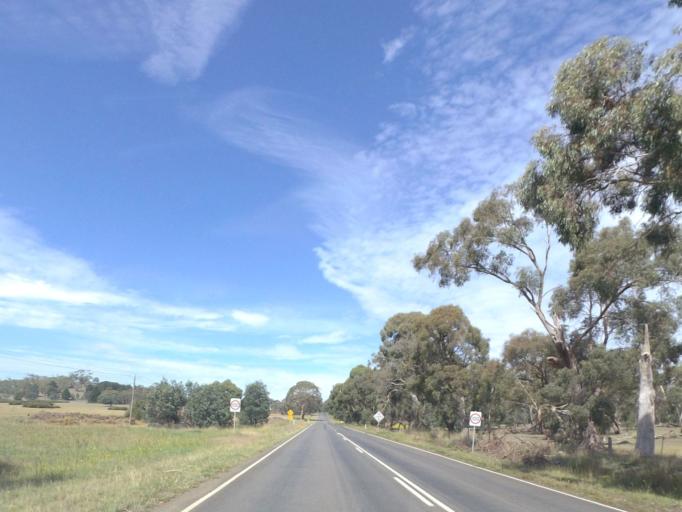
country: AU
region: Victoria
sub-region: Hume
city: Sunbury
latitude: -37.2942
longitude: 144.5084
